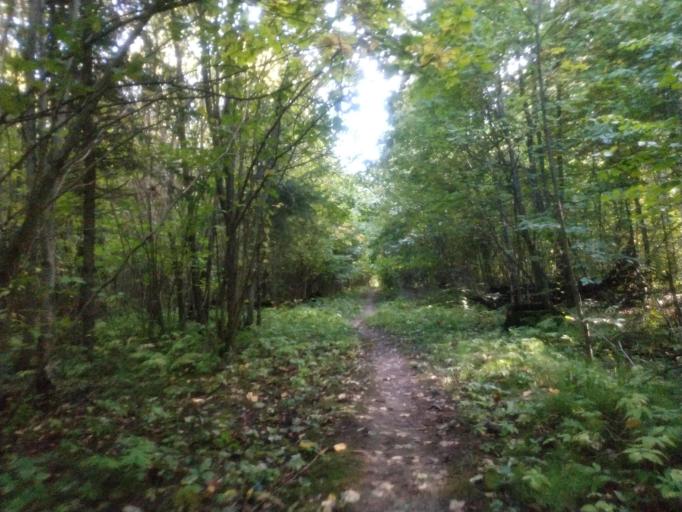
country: RU
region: Chuvashia
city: Novyye Lapsary
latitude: 56.1339
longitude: 47.1113
